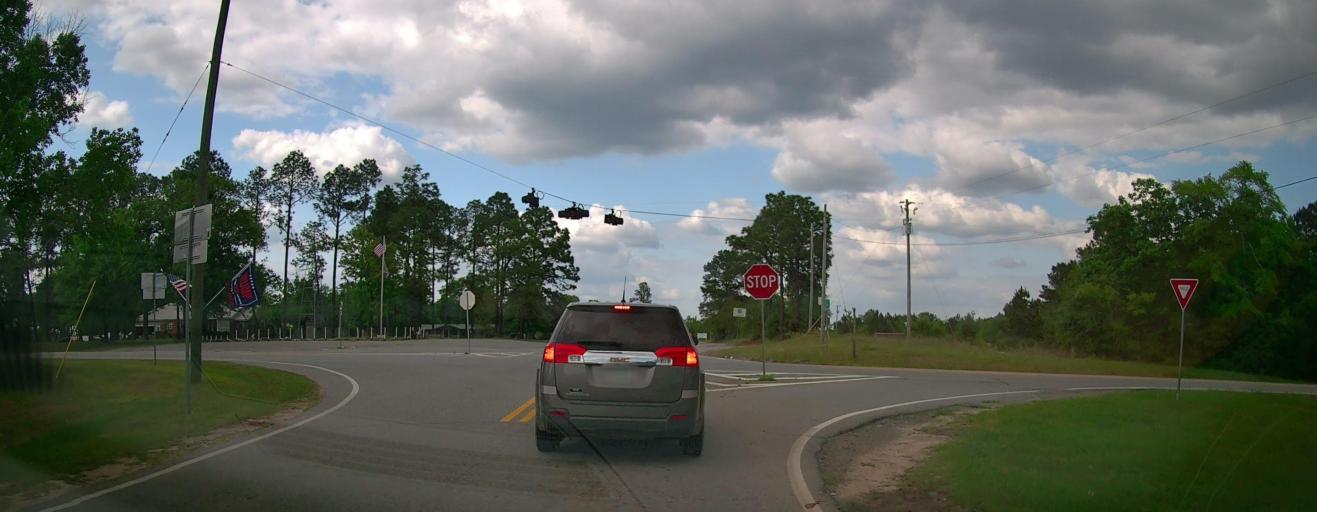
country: US
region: Georgia
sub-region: Washington County
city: Tennille
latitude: 32.7788
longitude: -82.9274
